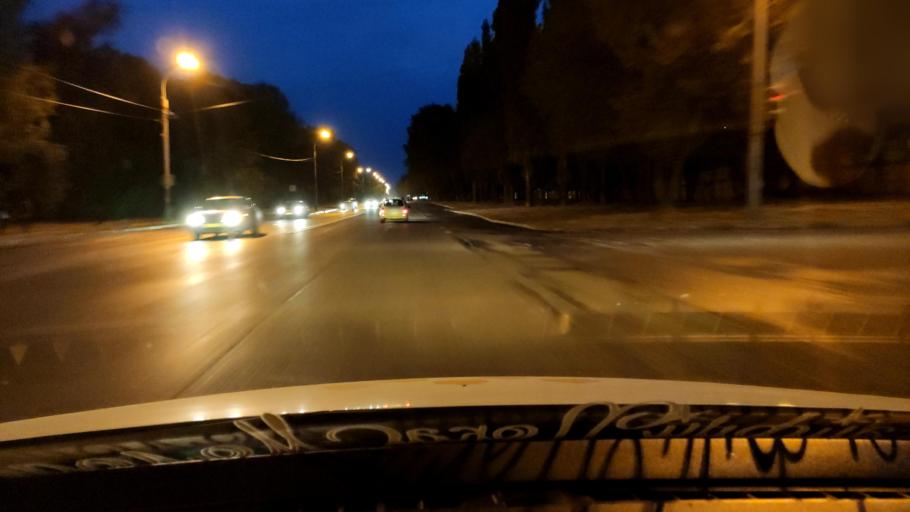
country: RU
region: Voronezj
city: Voronezh
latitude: 51.6513
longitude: 39.2117
